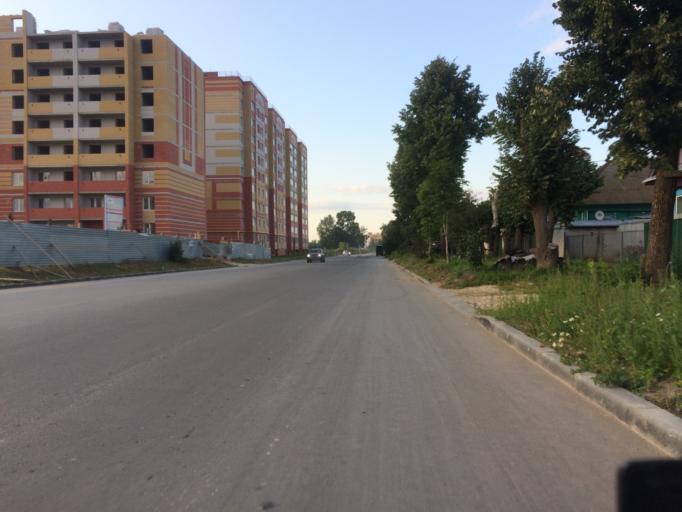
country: RU
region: Mariy-El
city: Medvedevo
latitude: 56.6496
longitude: 47.8372
